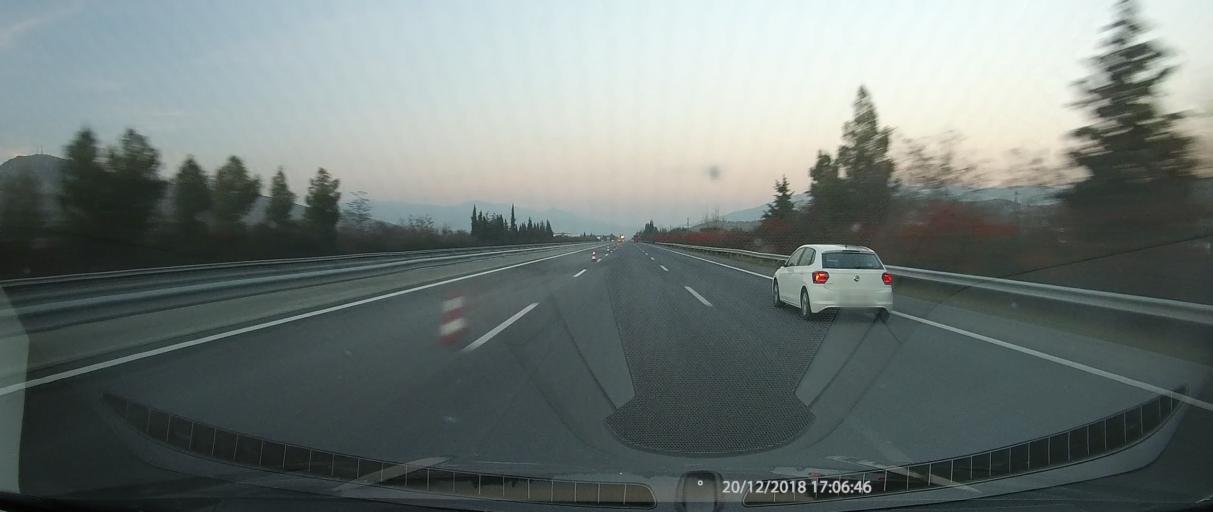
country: GR
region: Thessaly
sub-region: Nomos Larisis
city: Makrychori
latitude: 39.7652
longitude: 22.4814
